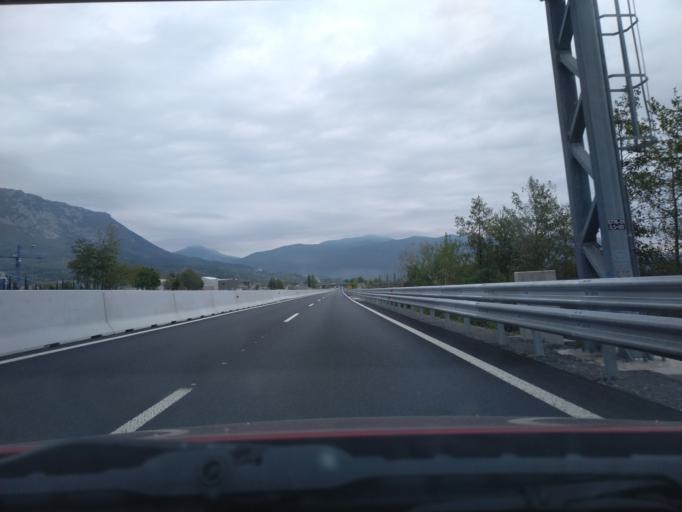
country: SI
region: Ajdovscina
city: Ajdovscina
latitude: 45.8818
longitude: 13.8948
